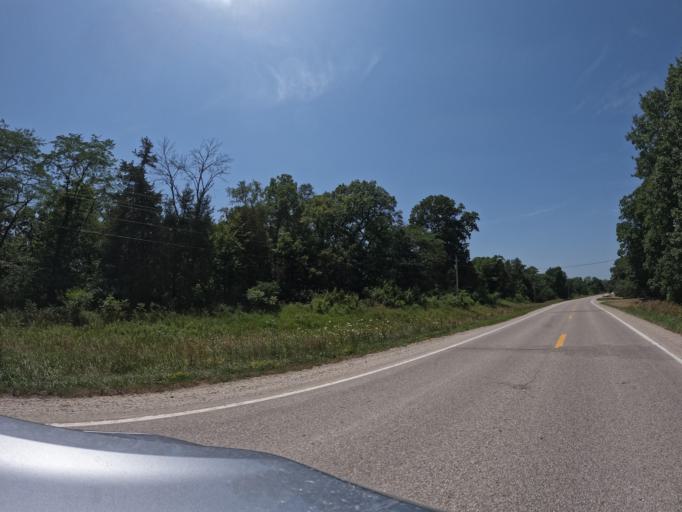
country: US
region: Iowa
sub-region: Henry County
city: Mount Pleasant
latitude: 40.9374
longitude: -91.5971
